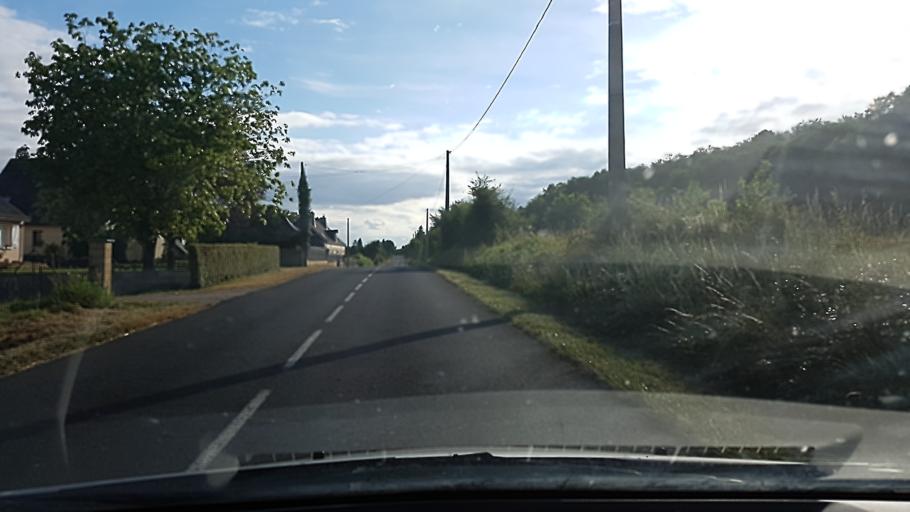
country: FR
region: Pays de la Loire
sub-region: Departement de Maine-et-Loire
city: Maze
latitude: 47.5001
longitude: -0.2585
